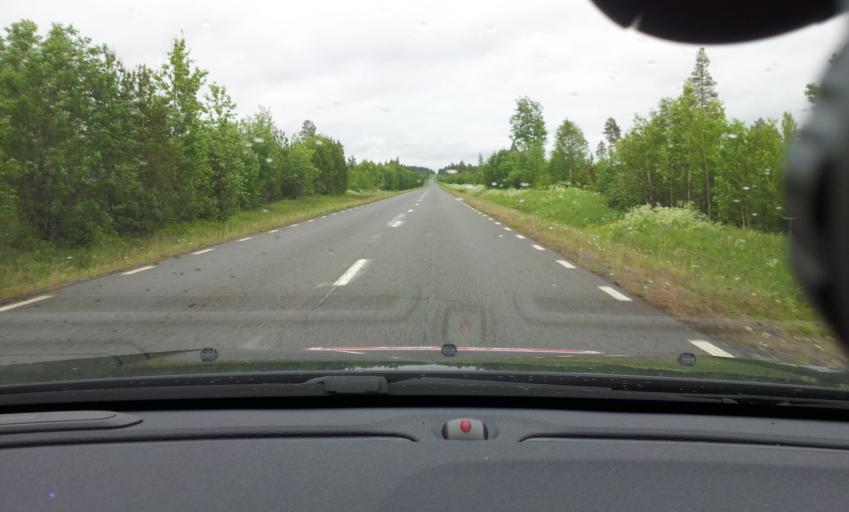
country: SE
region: Jaemtland
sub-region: OEstersunds Kommun
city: Lit
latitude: 63.7278
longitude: 14.9237
